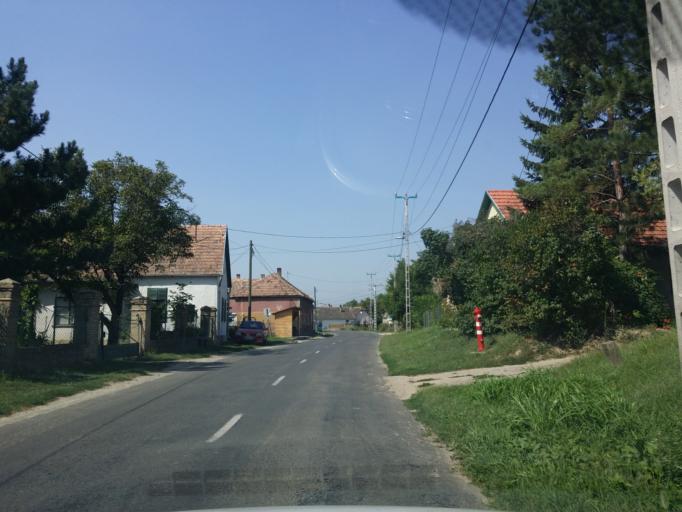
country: HU
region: Tolna
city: Gyonk
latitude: 46.6074
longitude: 18.4228
